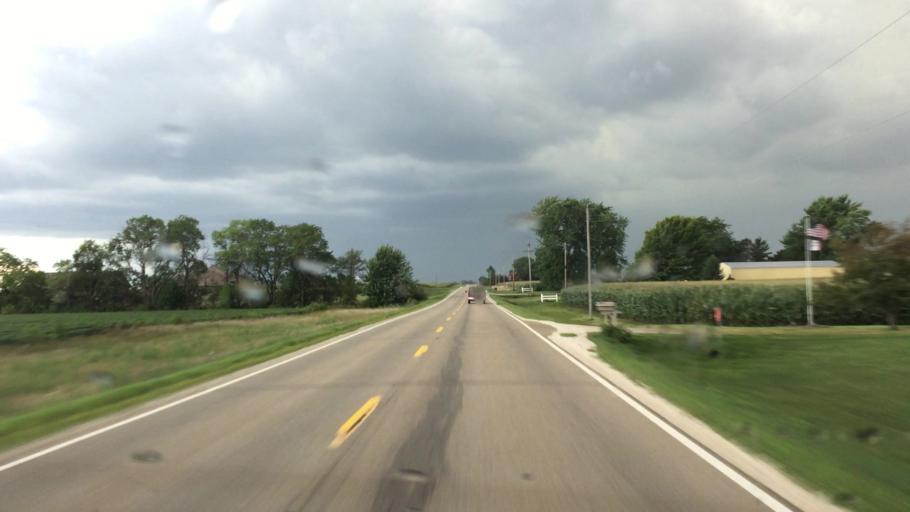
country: US
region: Iowa
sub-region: Henry County
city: New London
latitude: 40.7844
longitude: -91.5052
